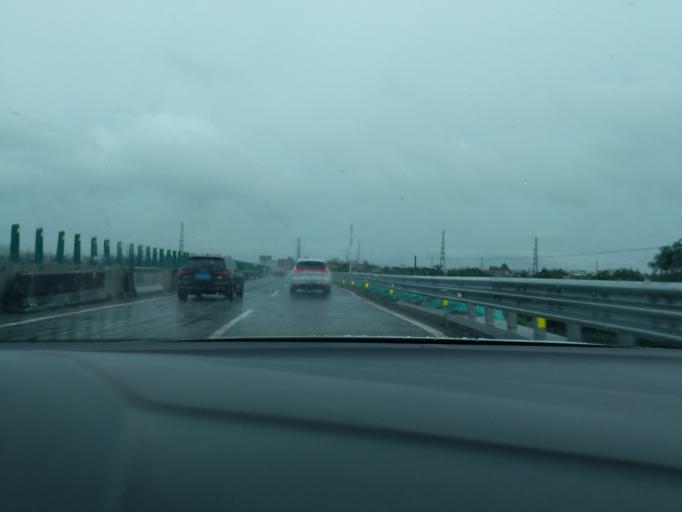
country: CN
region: Guangdong
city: Shuikou
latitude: 22.4677
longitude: 112.7553
